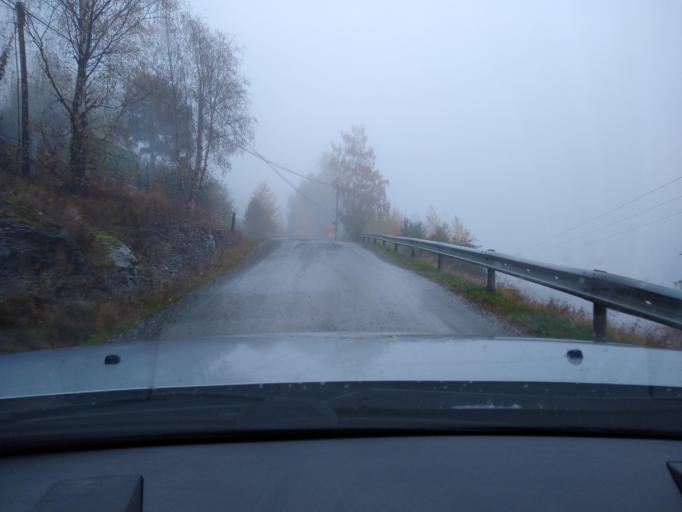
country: NO
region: Oppland
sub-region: Ringebu
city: Ringebu
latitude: 61.5264
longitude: 10.1611
